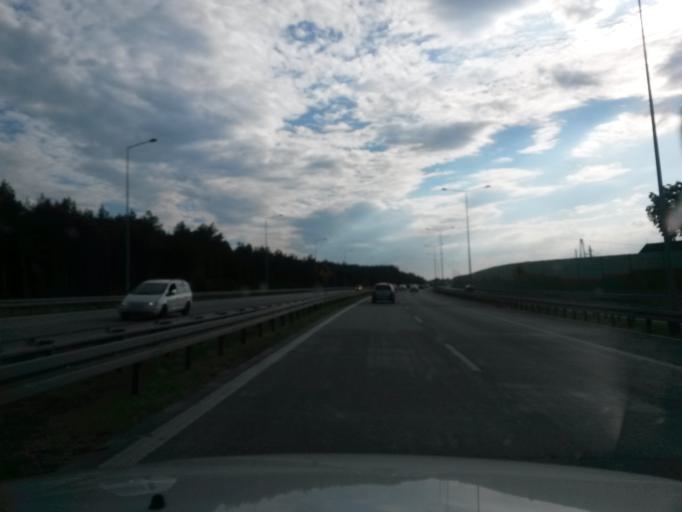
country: PL
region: Lodz Voivodeship
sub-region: Powiat tomaszowski
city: Tomaszow Mazowiecki
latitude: 51.5240
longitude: 19.9363
